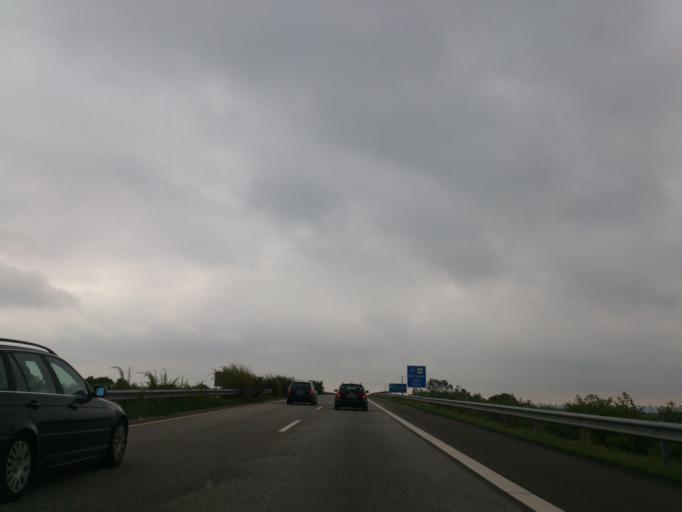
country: DE
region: Schleswig-Holstein
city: Schafstedt
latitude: 54.0709
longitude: 9.3091
